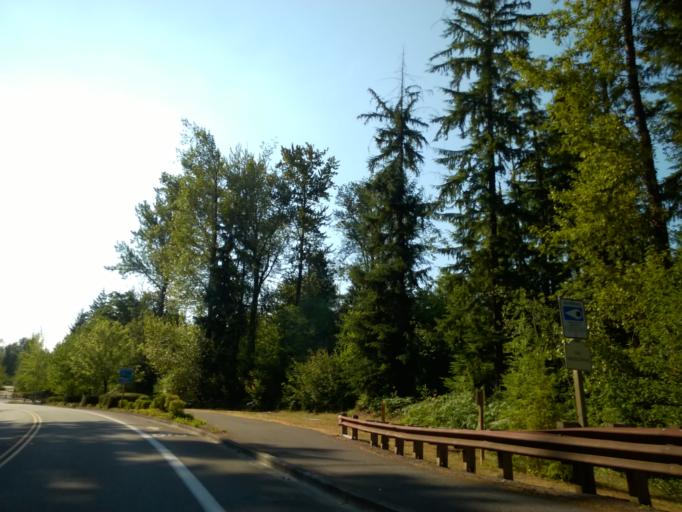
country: US
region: Washington
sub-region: King County
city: Union Hill-Novelty Hill
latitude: 47.6767
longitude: -122.0254
